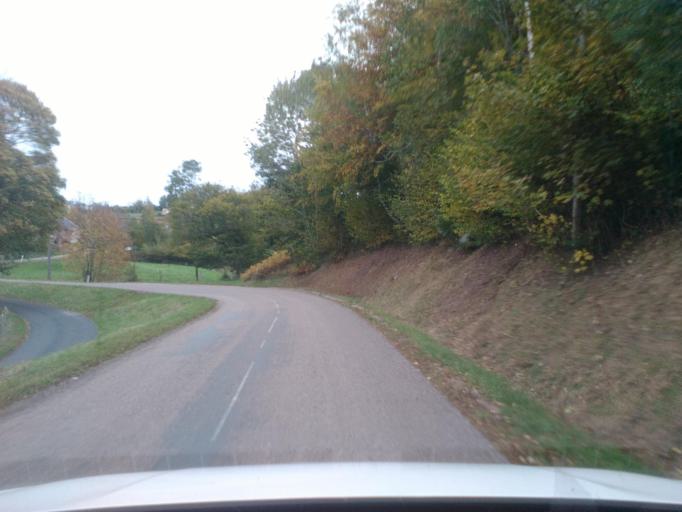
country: FR
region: Lorraine
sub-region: Departement des Vosges
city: Senones
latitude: 48.3383
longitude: 7.0099
